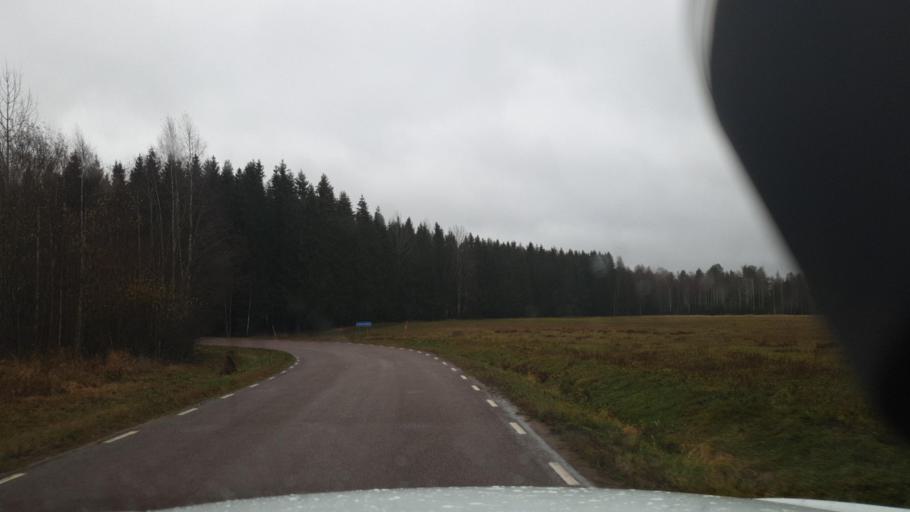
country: SE
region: Vaermland
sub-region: Sunne Kommun
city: Sunne
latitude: 59.7403
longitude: 13.0659
